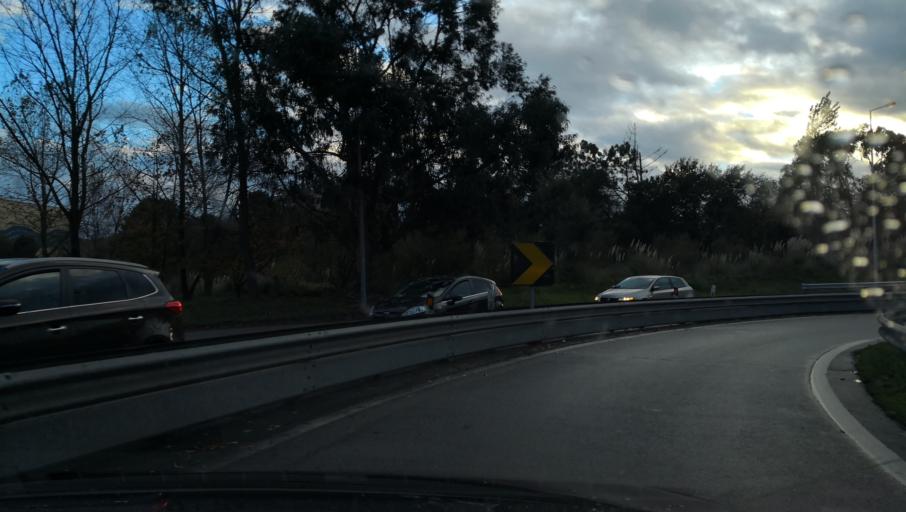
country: PT
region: Porto
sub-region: Vila Nova de Gaia
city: Vila Nova de Gaia
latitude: 41.1192
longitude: -8.6236
